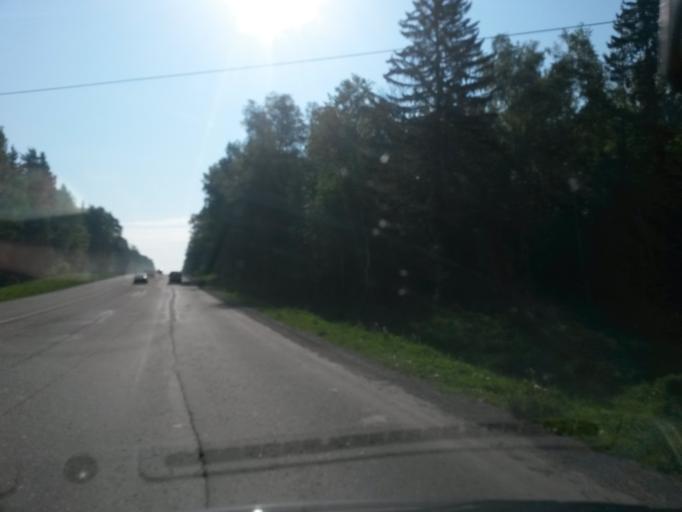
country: RU
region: Jaroslavl
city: Pereslavl'-Zalesskiy
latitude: 56.8701
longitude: 38.9727
